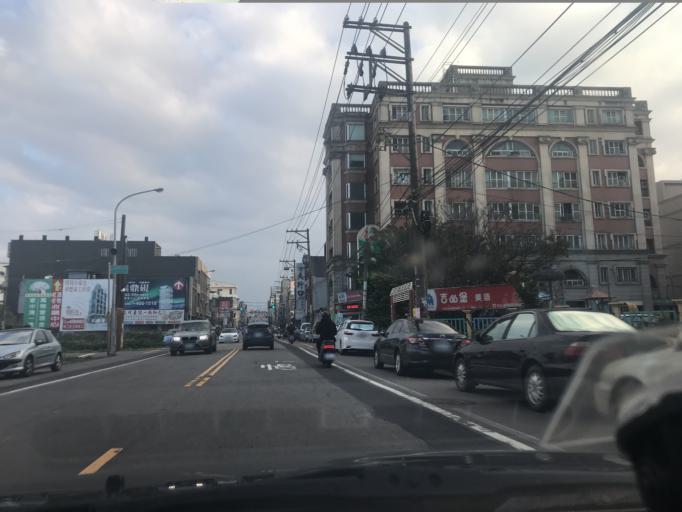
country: TW
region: Taiwan
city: Taoyuan City
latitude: 24.9605
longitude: 121.2318
